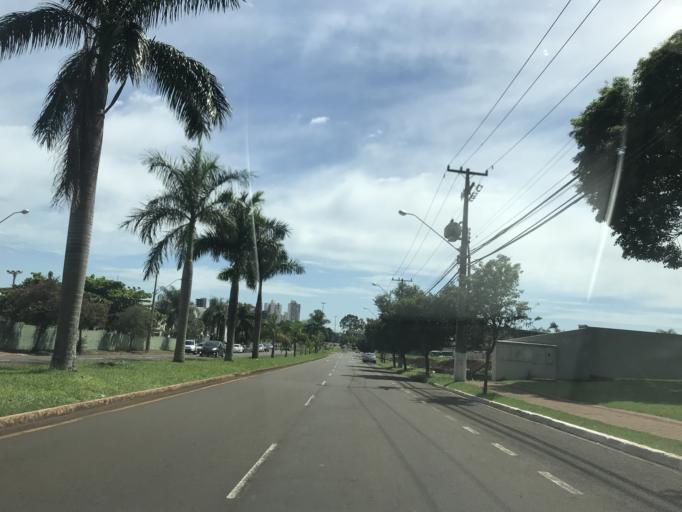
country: BR
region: Parana
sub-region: Londrina
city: Londrina
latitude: -23.3444
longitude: -51.1616
